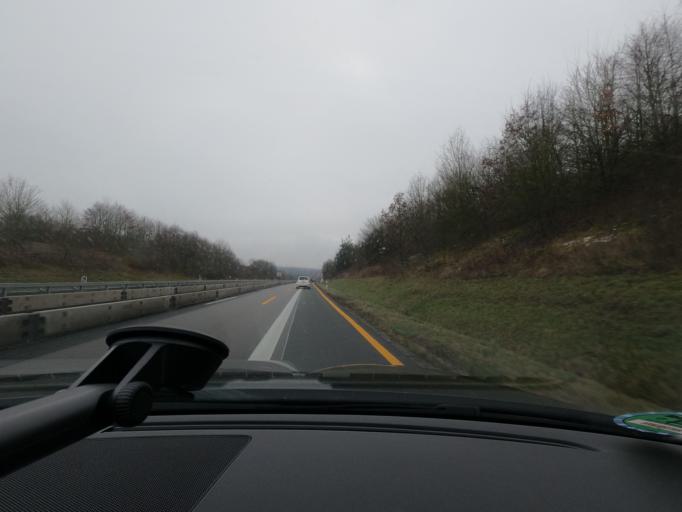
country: DE
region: Bavaria
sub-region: Upper Franconia
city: Strullendorf
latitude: 49.8457
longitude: 10.9957
